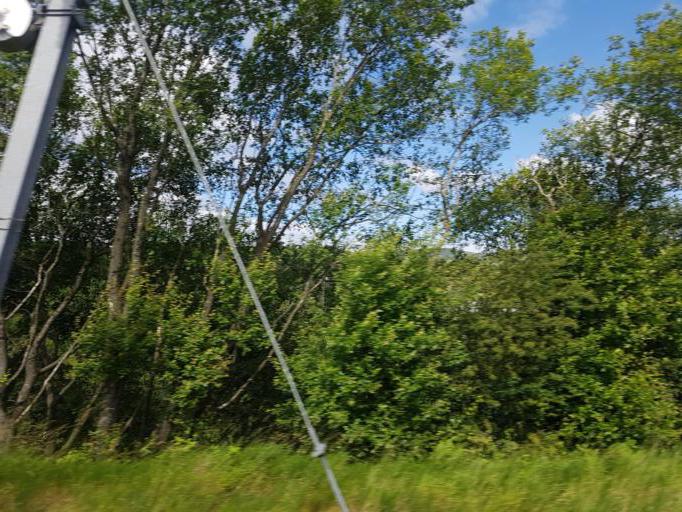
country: GB
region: Scotland
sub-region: North Lanarkshire
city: Kilsyth
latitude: 55.9498
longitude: -4.0546
